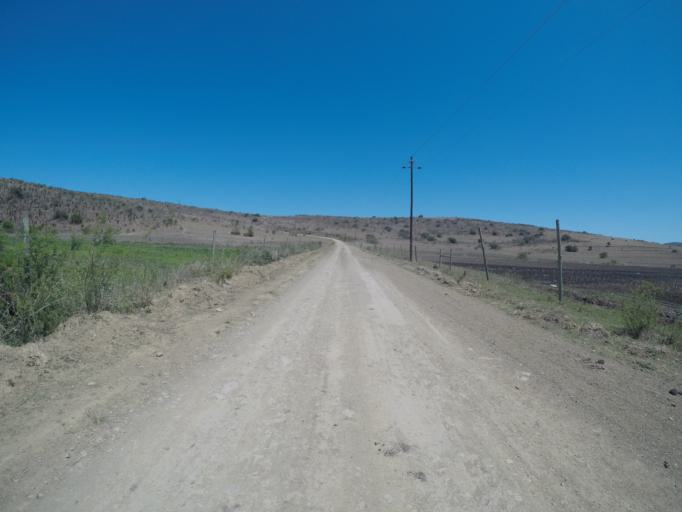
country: ZA
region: Eastern Cape
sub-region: OR Tambo District Municipality
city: Mthatha
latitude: -31.8710
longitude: 28.8695
